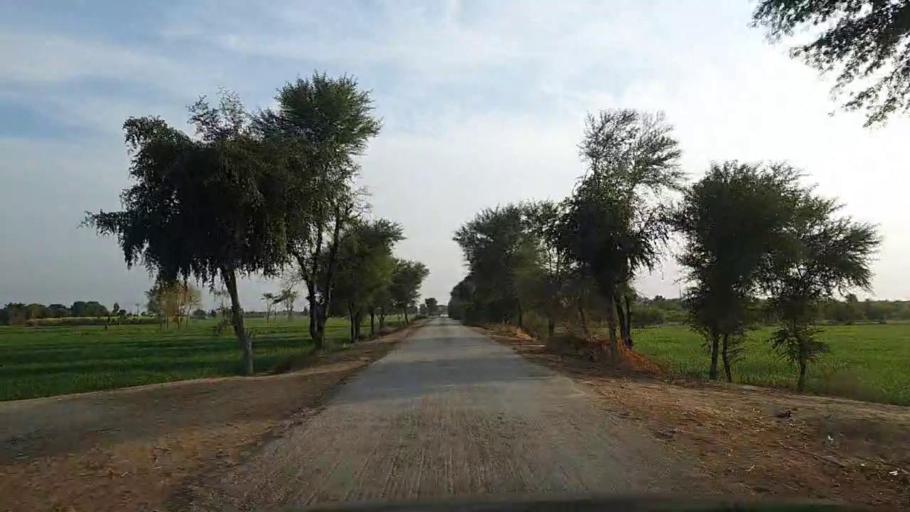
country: PK
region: Sindh
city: Jam Sahib
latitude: 26.4359
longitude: 68.5715
